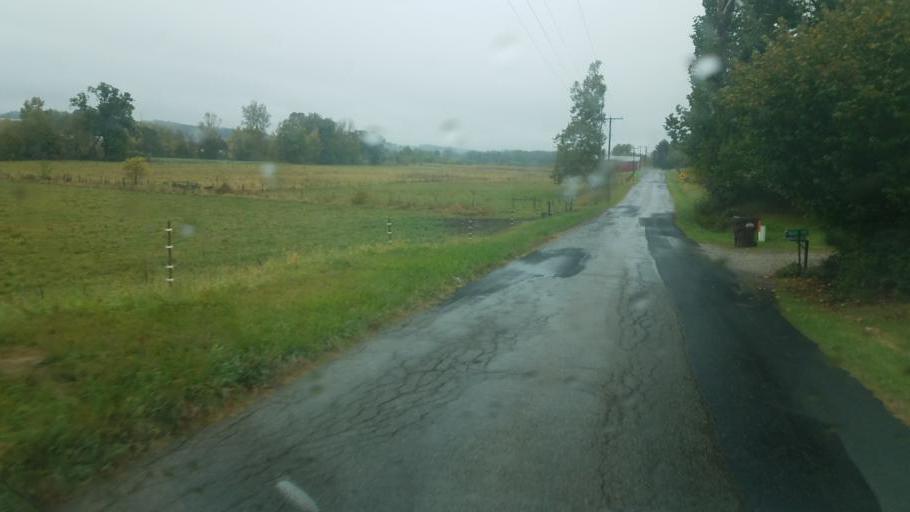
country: US
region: Ohio
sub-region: Knox County
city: Danville
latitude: 40.4933
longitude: -82.2883
